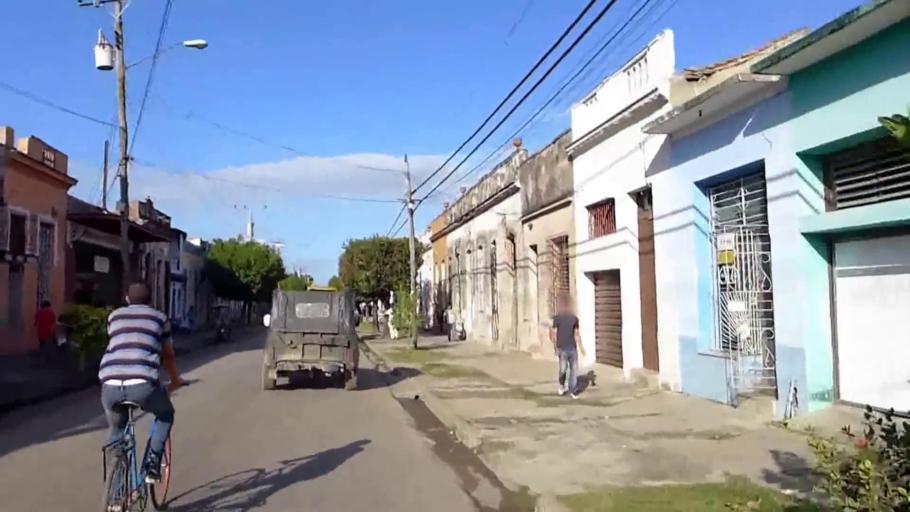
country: CU
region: Camaguey
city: Camaguey
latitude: 21.3848
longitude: -77.9261
